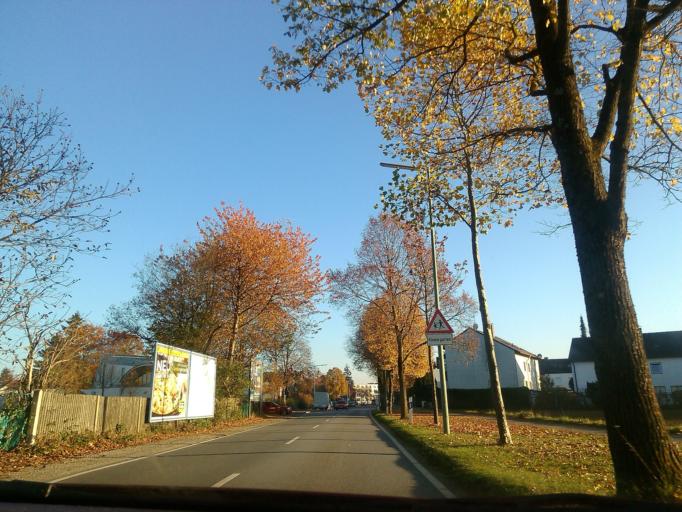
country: DE
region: Bavaria
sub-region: Upper Bavaria
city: Pasing
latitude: 48.1300
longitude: 11.4725
